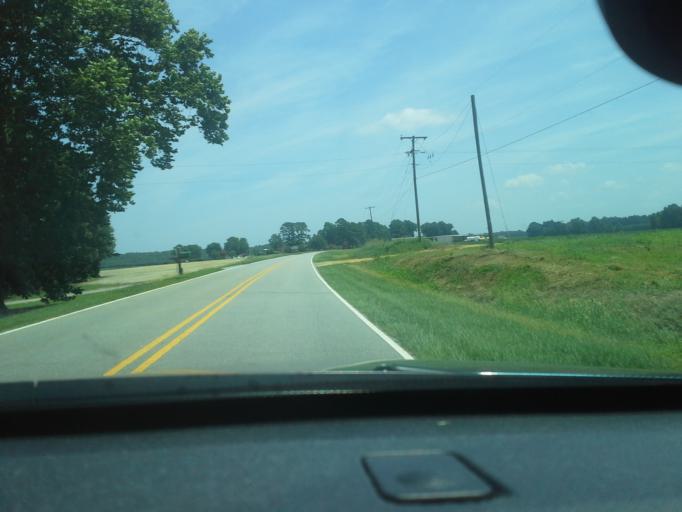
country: US
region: North Carolina
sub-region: Washington County
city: Plymouth
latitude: 35.9197
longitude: -76.6436
